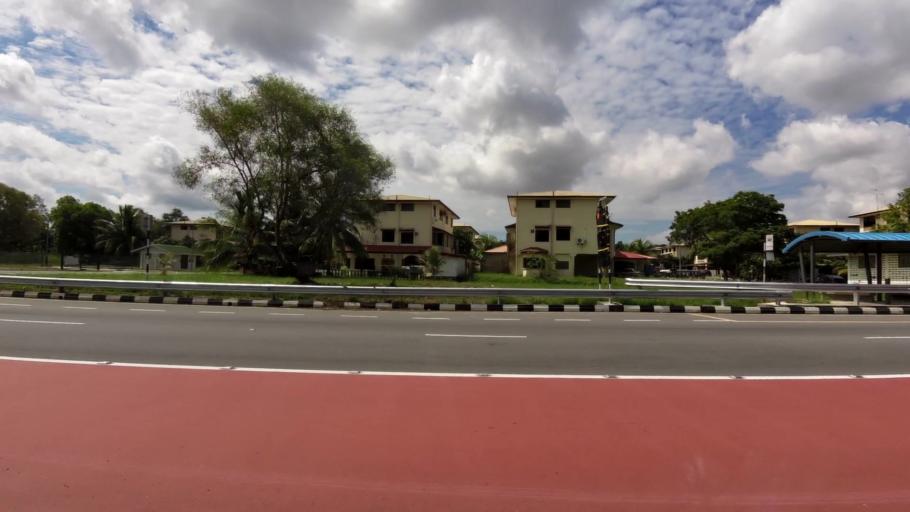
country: BN
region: Brunei and Muara
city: Bandar Seri Begawan
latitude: 4.9340
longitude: 114.8956
